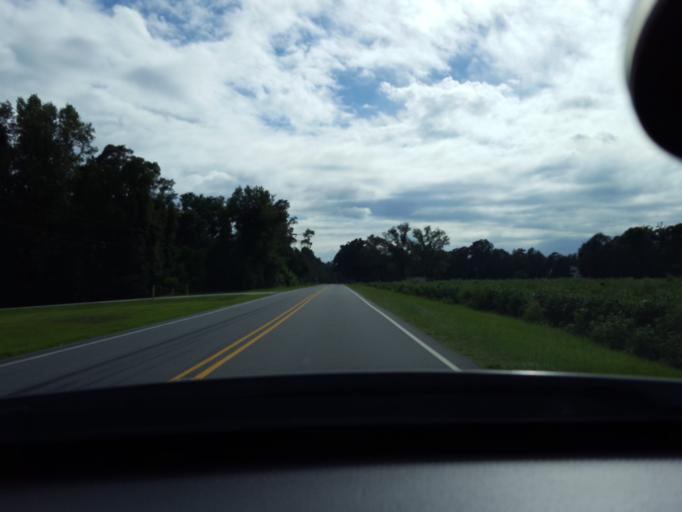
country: US
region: North Carolina
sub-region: Duplin County
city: Kenansville
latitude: 35.0191
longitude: -77.8639
